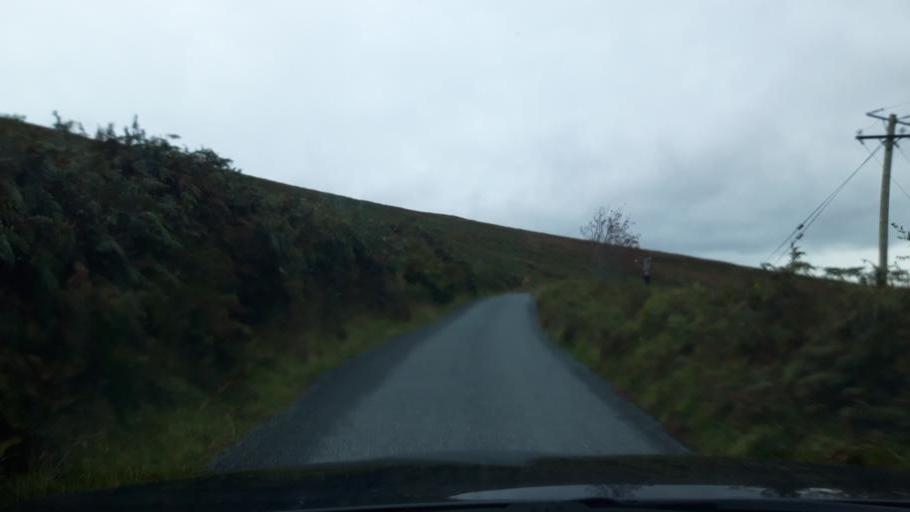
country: IE
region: Leinster
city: Ballinteer
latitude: 53.1919
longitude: -6.2928
